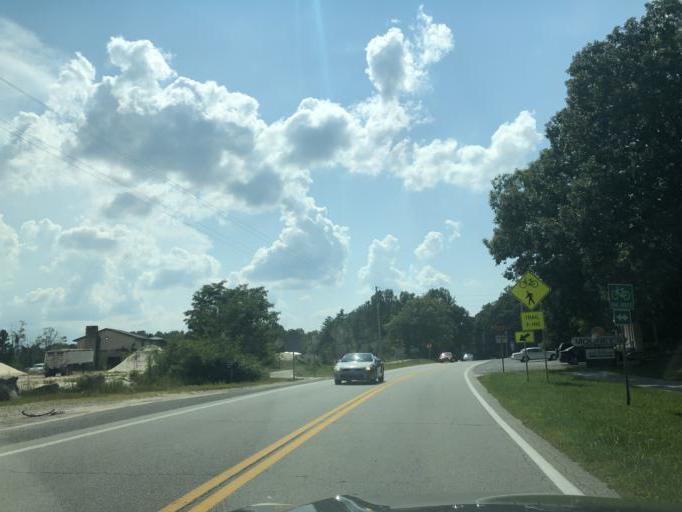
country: US
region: Tennessee
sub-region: Marion County
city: Monteagle
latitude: 35.2238
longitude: -85.8722
